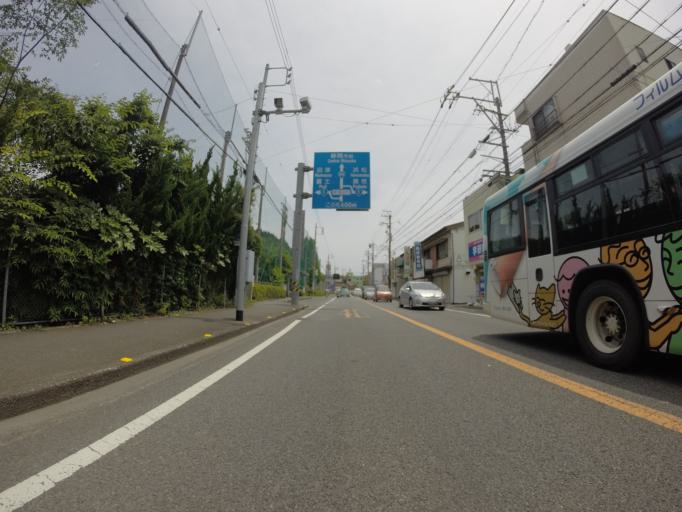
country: JP
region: Shizuoka
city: Shizuoka-shi
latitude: 34.9801
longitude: 138.3437
